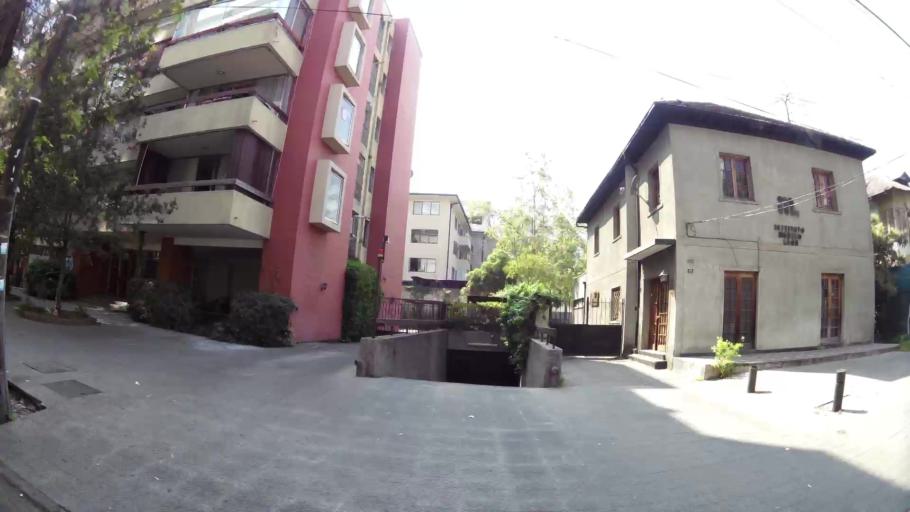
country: CL
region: Santiago Metropolitan
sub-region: Provincia de Santiago
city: Villa Presidente Frei, Nunoa, Santiago, Chile
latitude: -33.4250
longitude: -70.6098
